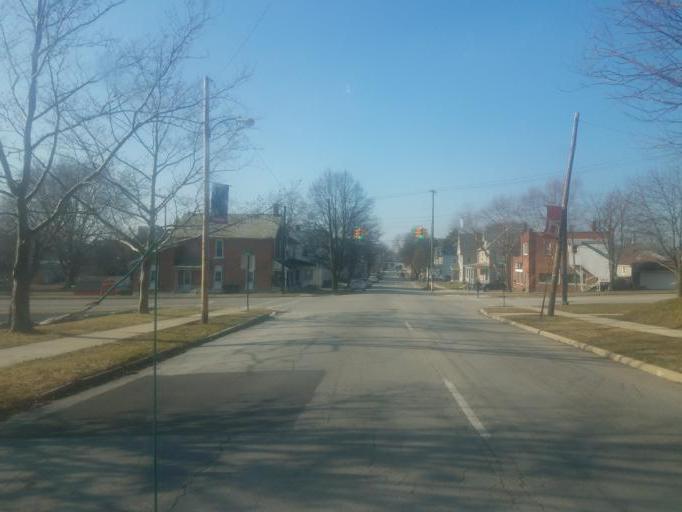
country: US
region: Ohio
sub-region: Seneca County
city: Tiffin
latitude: 41.1164
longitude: -83.1703
